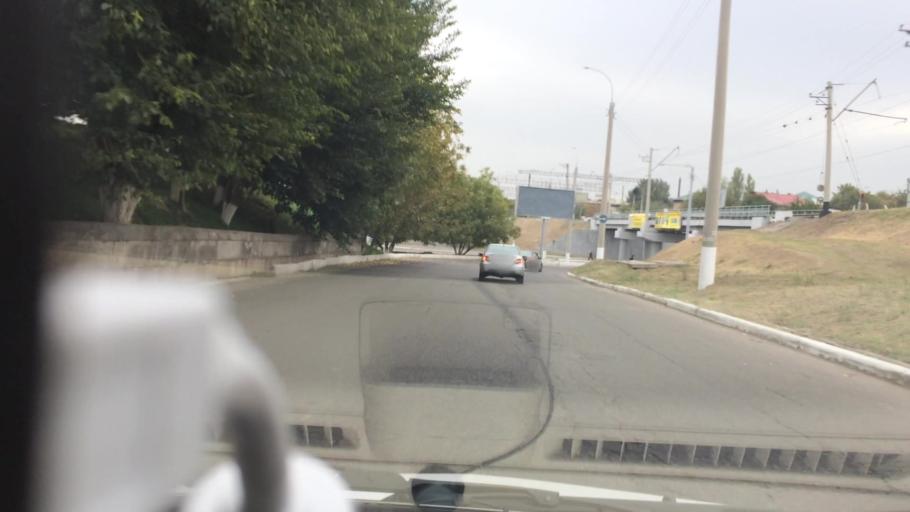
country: UZ
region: Toshkent
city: Salor
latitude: 41.3178
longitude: 69.3115
